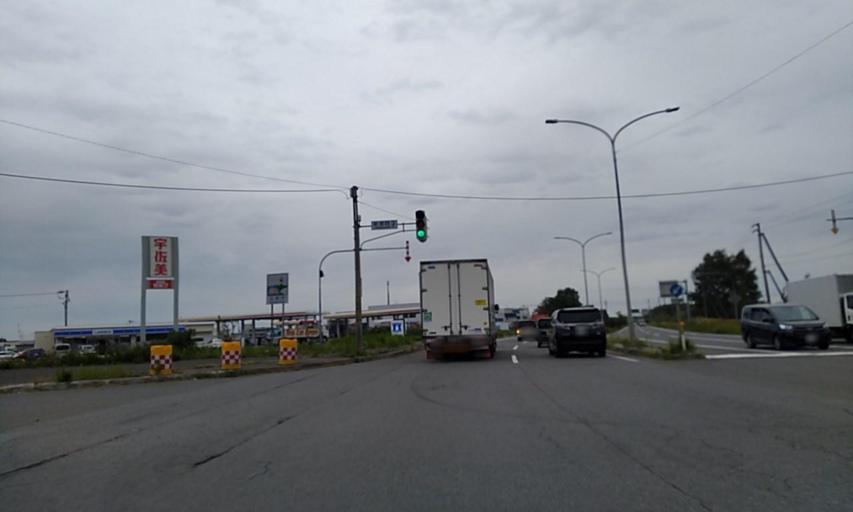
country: JP
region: Hokkaido
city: Ishikari
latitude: 43.1605
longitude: 141.2498
